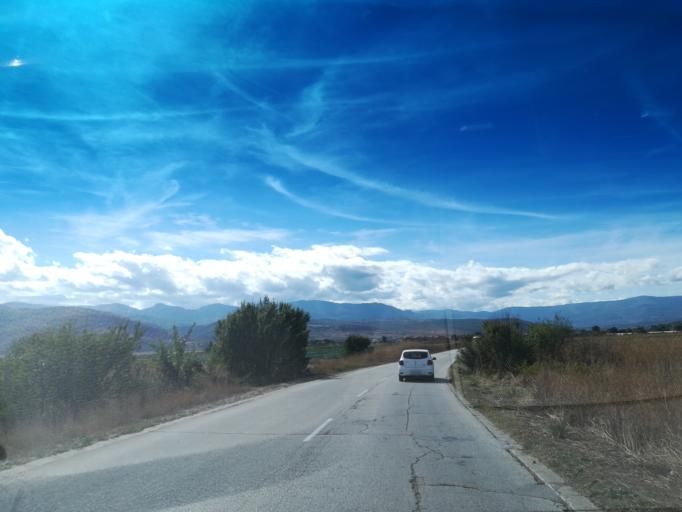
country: BG
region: Plovdiv
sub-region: Obshtina Krichim
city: Krichim
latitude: 42.0910
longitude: 24.4462
